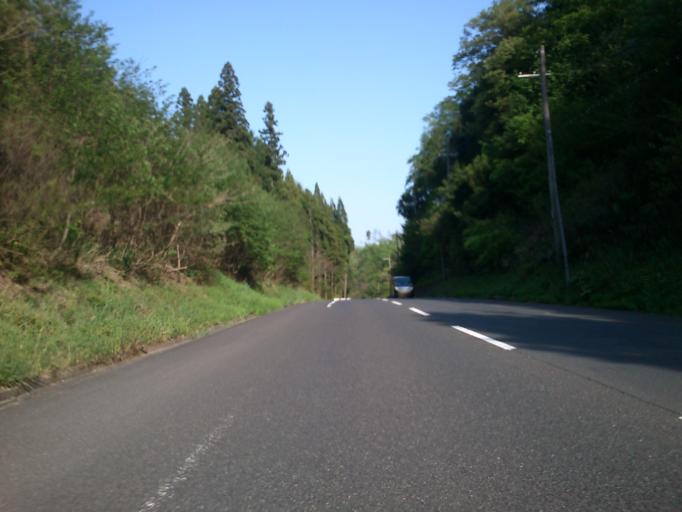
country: JP
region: Kyoto
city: Miyazu
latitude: 35.5938
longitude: 135.1486
